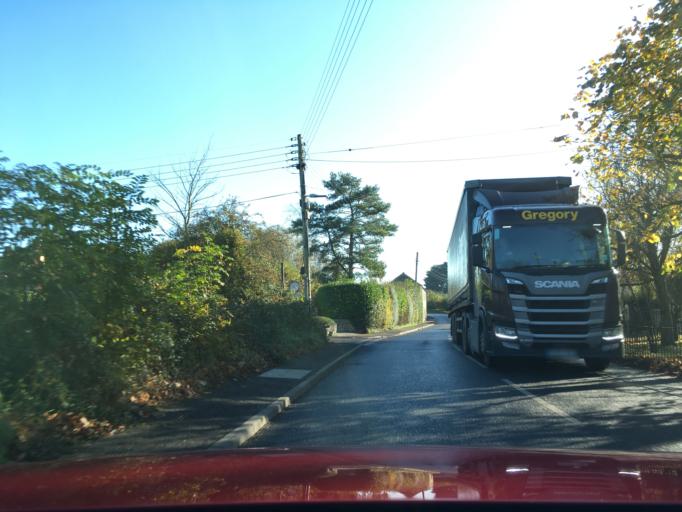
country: GB
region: England
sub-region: Somerset
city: Langport
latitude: 51.0354
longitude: -2.8111
